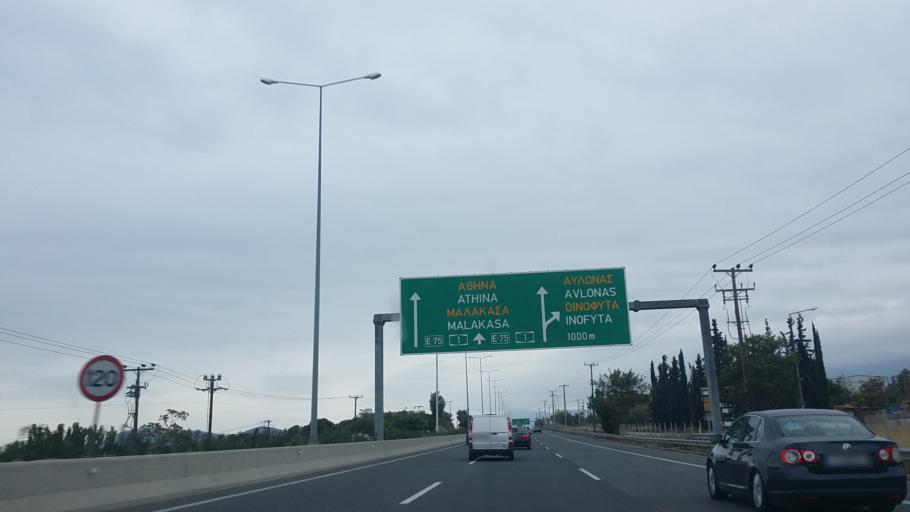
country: GR
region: Central Greece
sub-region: Nomos Voiotias
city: Oinofyta
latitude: 38.2971
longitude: 23.6648
